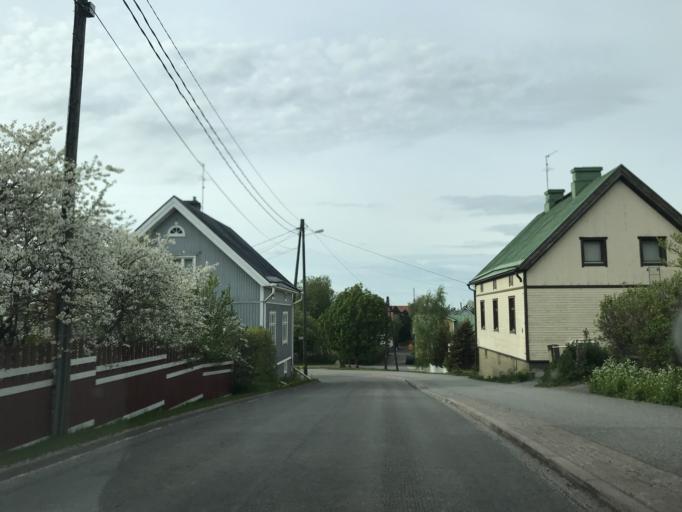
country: FI
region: Varsinais-Suomi
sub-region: Turku
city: Turku
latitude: 60.4536
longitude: 22.3078
